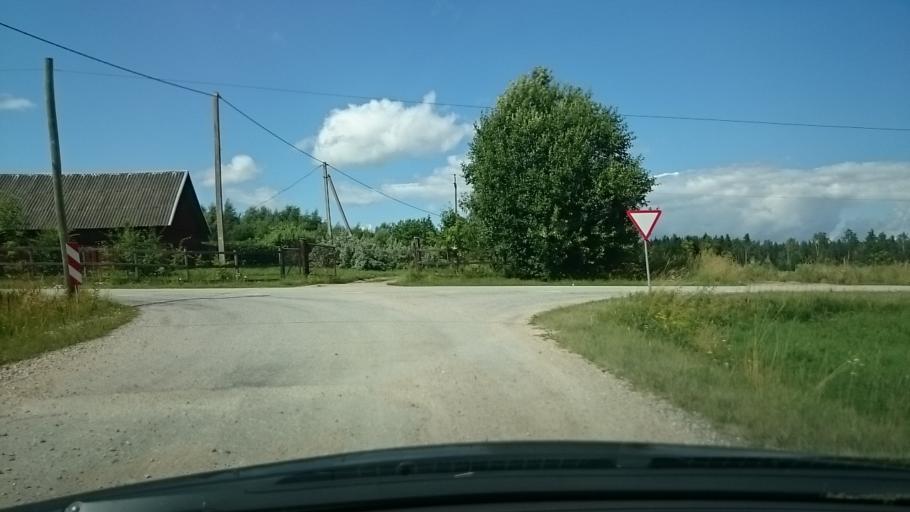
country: EE
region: Polvamaa
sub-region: Polva linn
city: Polva
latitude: 57.9759
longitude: 27.0084
